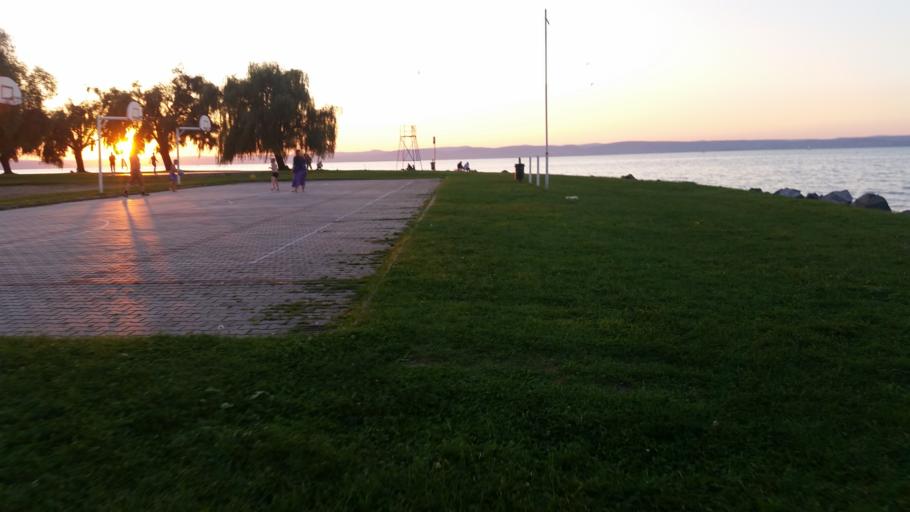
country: HU
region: Somogy
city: Siofok
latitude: 46.9044
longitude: 18.0278
